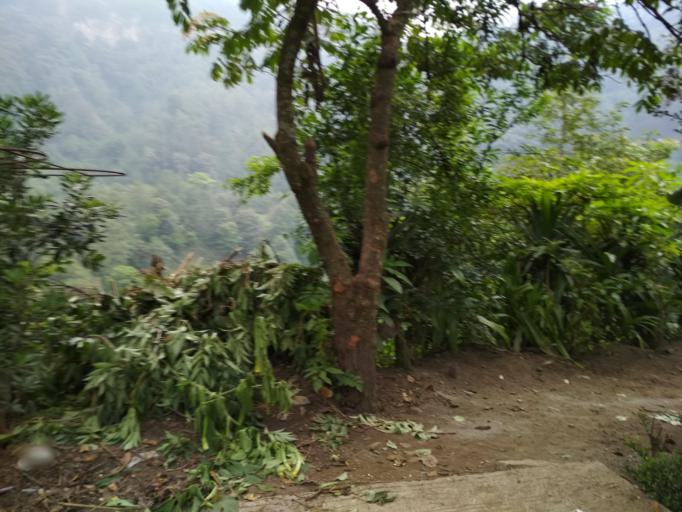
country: MX
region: Veracruz
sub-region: La Perla
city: Metlac Hernandez (Metlac Primero)
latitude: 18.9803
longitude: -97.1363
